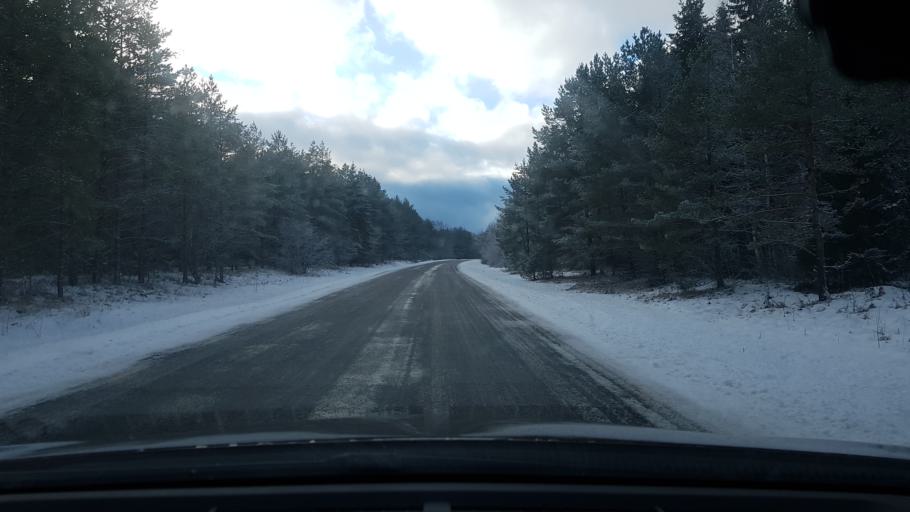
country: EE
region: Harju
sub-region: Paldiski linn
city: Paldiski
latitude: 59.2929
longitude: 24.1581
